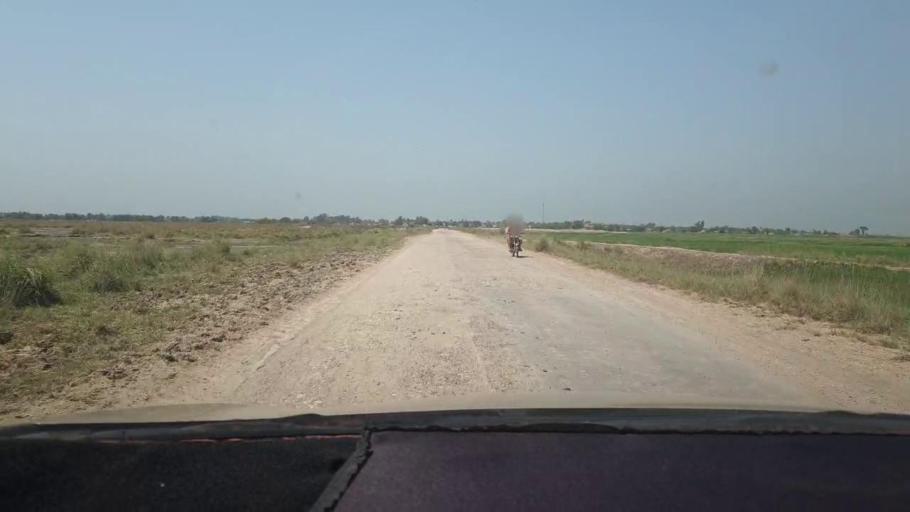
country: PK
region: Sindh
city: Miro Khan
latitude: 27.6643
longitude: 68.0713
